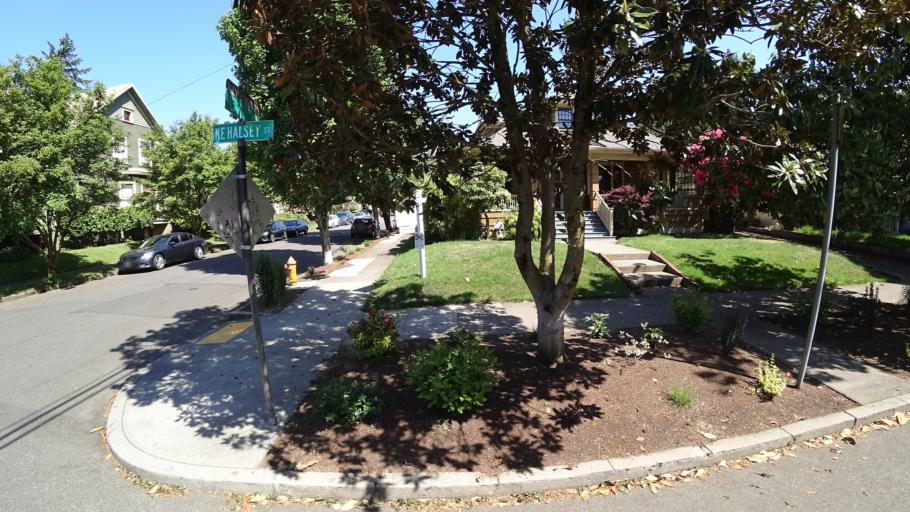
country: US
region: Oregon
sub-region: Multnomah County
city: Portland
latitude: 45.5338
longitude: -122.6381
